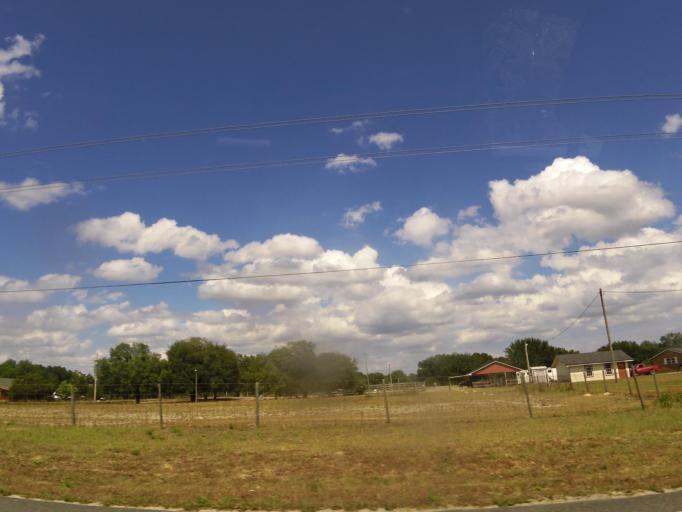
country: US
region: Florida
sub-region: Clay County
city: Keystone Heights
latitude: 29.8346
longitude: -81.9225
